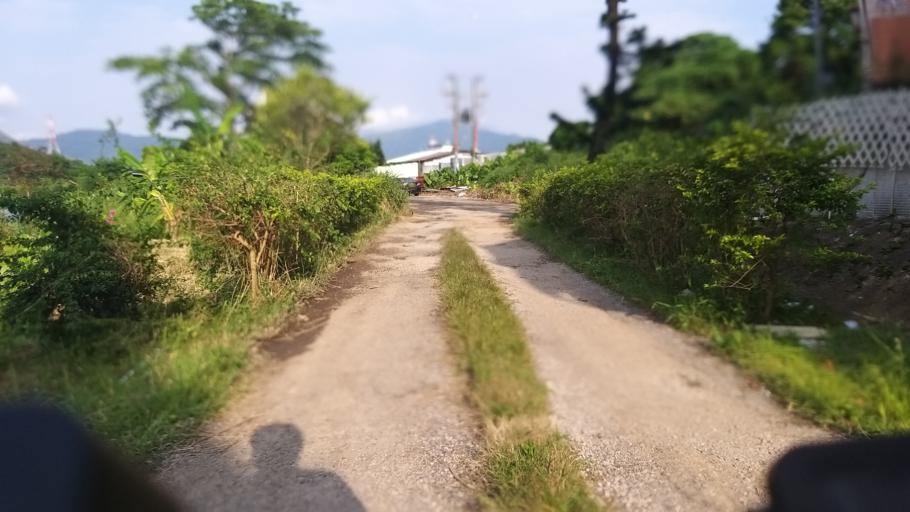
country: HK
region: Yuen Long
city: Yuen Long Kau Hui
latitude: 22.4536
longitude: 114.0387
